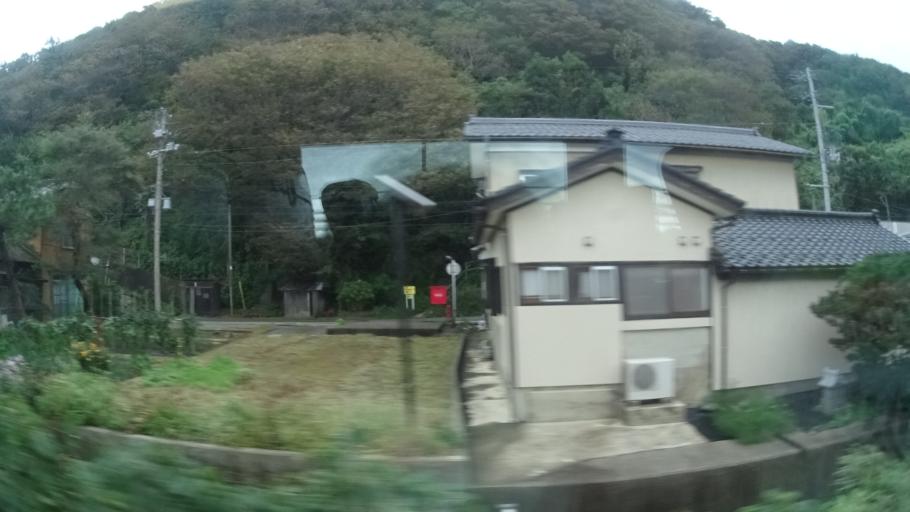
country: JP
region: Yamagata
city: Tsuruoka
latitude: 38.6085
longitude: 139.5754
